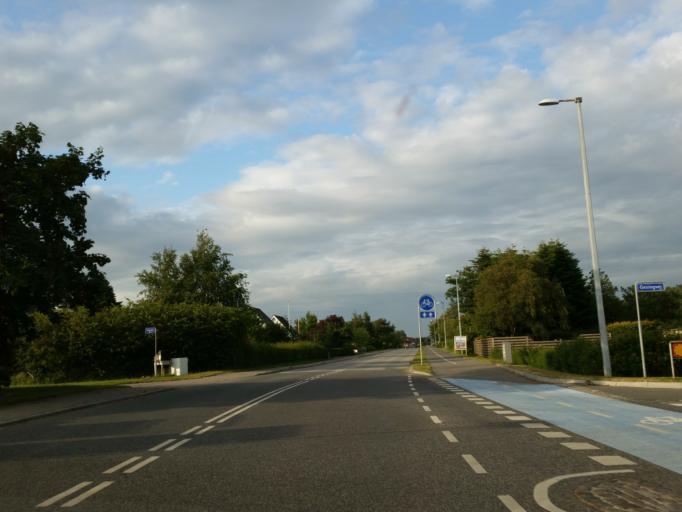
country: DK
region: South Denmark
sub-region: Tonder Kommune
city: Sherrebek
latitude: 55.1518
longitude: 8.7561
